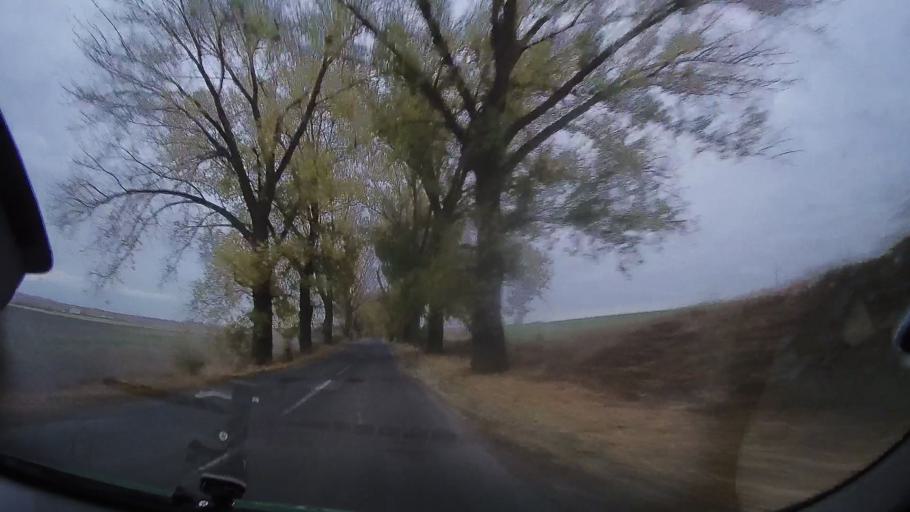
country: RO
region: Tulcea
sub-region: Comuna Mihai Bravu
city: Turda
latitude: 44.9654
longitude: 28.6349
